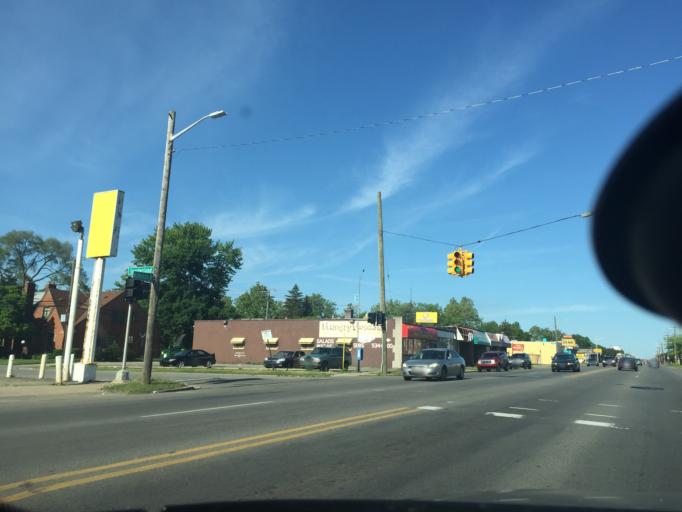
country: US
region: Michigan
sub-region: Oakland County
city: Southfield
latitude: 42.4153
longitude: -83.2282
